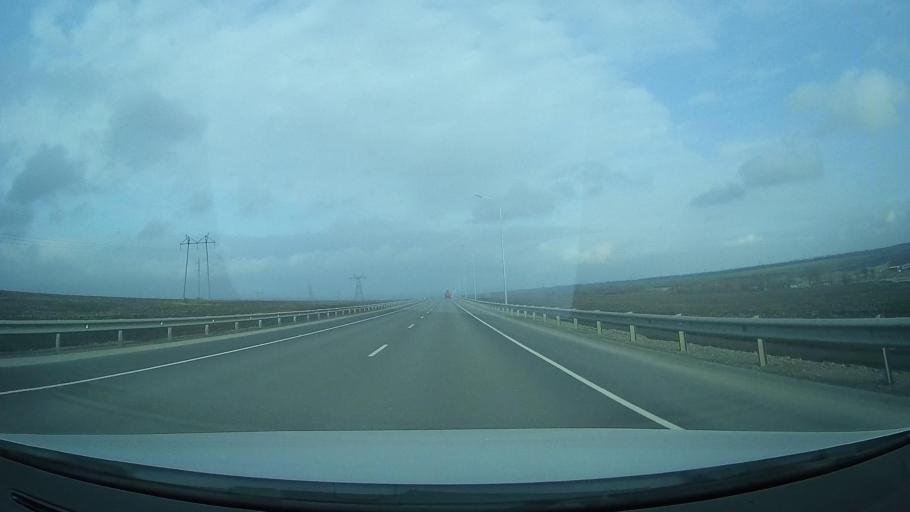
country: RU
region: Rostov
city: Grushevskaya
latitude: 47.3932
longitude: 39.8489
